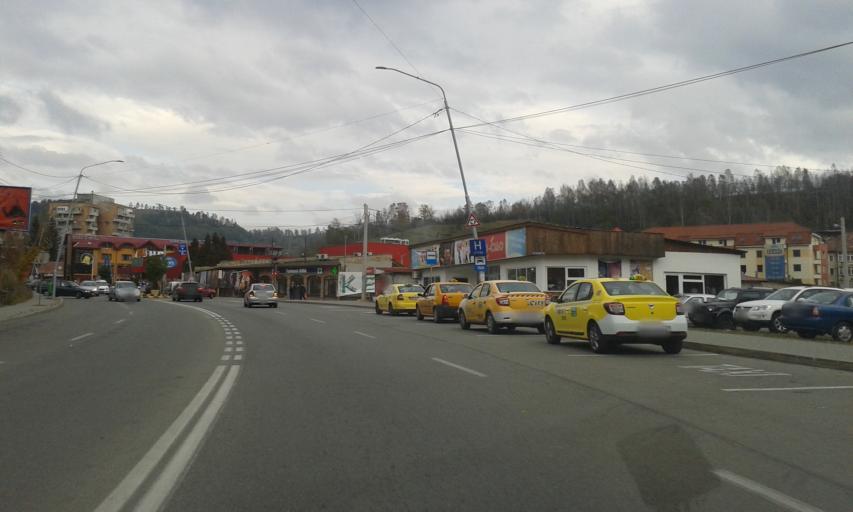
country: RO
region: Hunedoara
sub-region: Municipiul Petrosani
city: Petrosani
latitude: 45.4084
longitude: 23.3748
